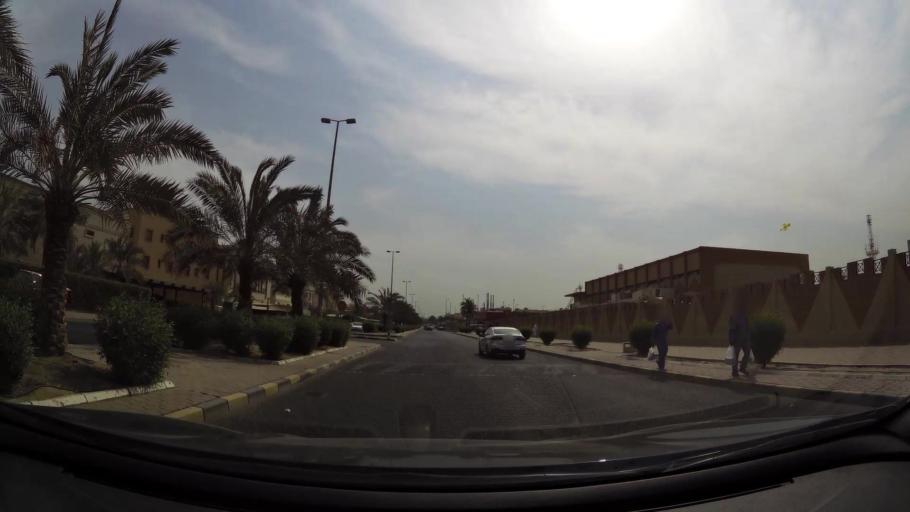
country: KW
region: Al Asimah
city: Ash Shamiyah
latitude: 29.3403
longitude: 47.9805
